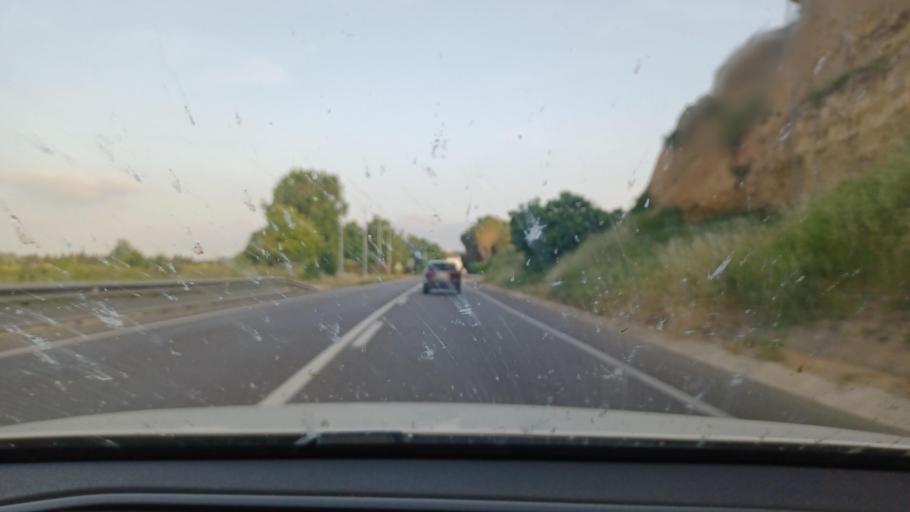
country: ES
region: Catalonia
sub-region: Provincia de Tarragona
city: Tortosa
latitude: 40.7852
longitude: 0.5015
